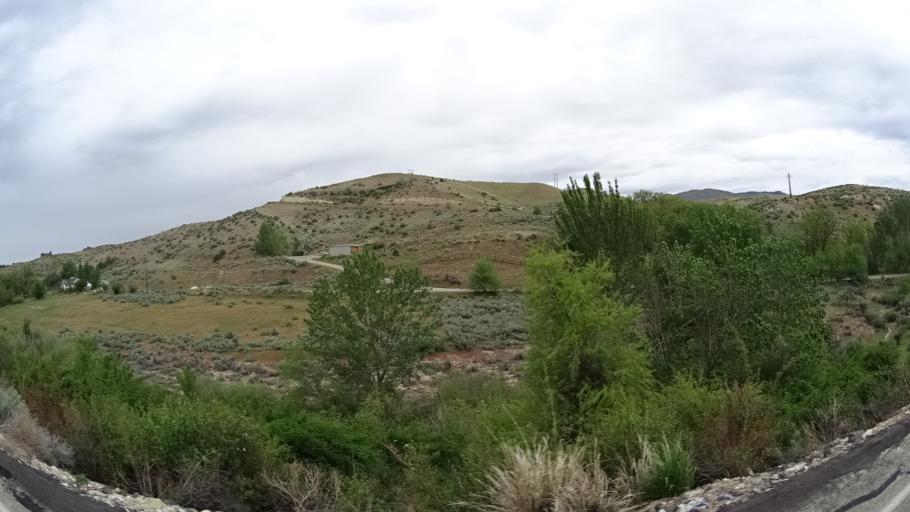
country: US
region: Idaho
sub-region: Ada County
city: Boise
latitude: 43.6160
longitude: -116.1617
